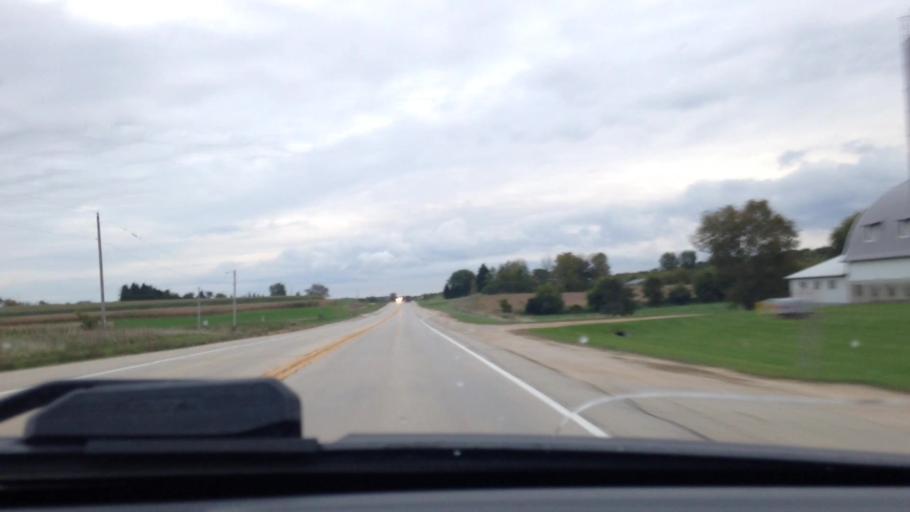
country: US
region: Wisconsin
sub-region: Dodge County
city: Mayville
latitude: 43.5150
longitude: -88.5238
